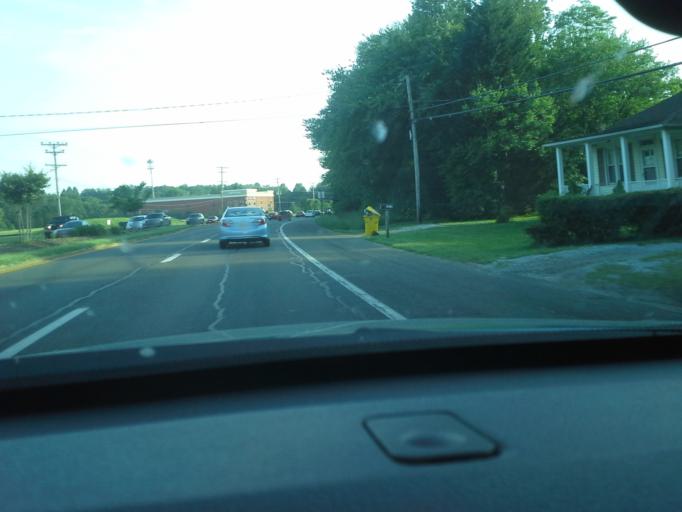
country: US
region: Maryland
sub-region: Anne Arundel County
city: Edgewater
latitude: 38.9620
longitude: -76.5470
